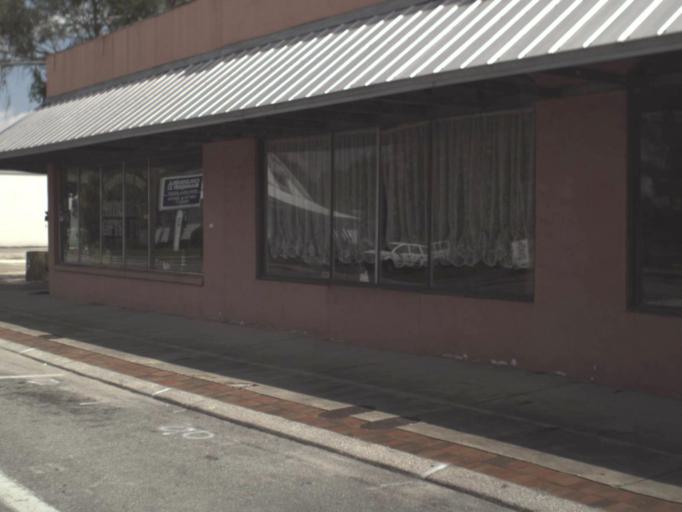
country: US
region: Florida
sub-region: Bradford County
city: Starke
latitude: 29.9437
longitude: -82.1083
